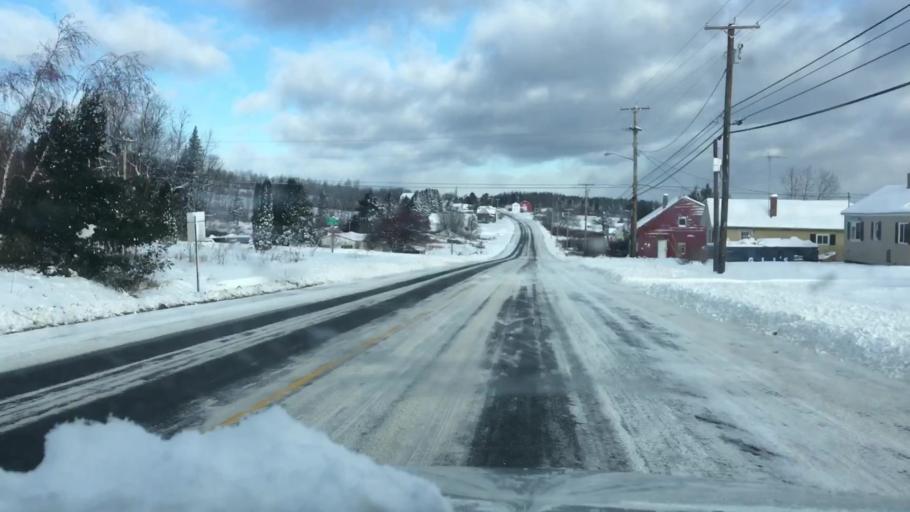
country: US
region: Maine
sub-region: Aroostook County
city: Caribou
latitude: 46.9556
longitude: -68.0278
